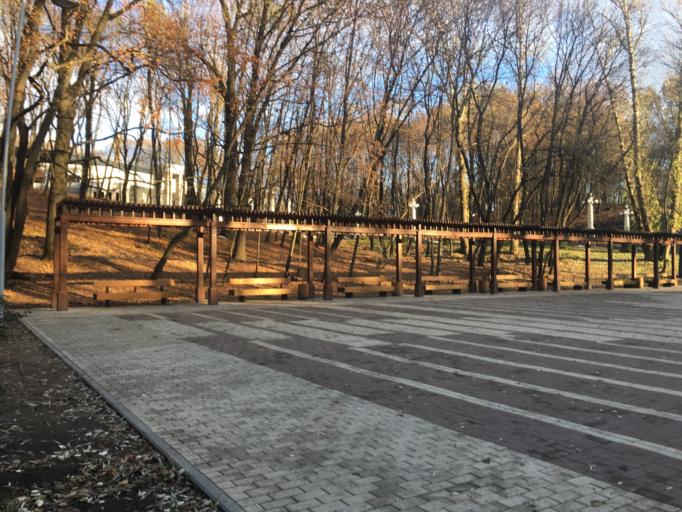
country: RU
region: Voronezj
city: Voronezh
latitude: 51.6996
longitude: 39.2188
